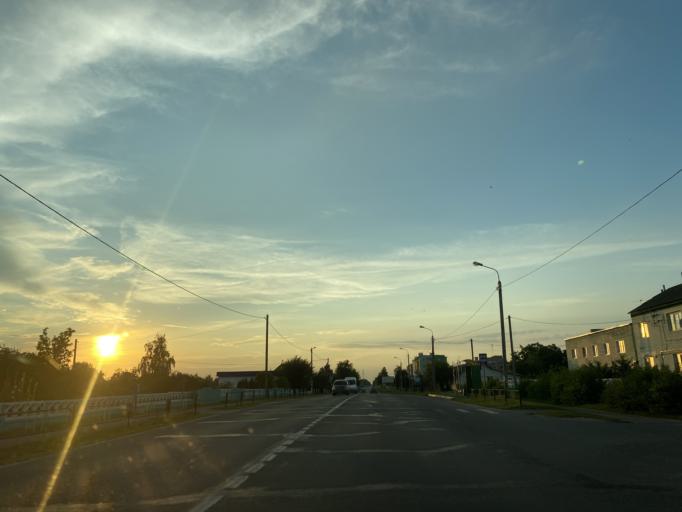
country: BY
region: Brest
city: Ivatsevichy
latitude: 52.7052
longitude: 25.3583
